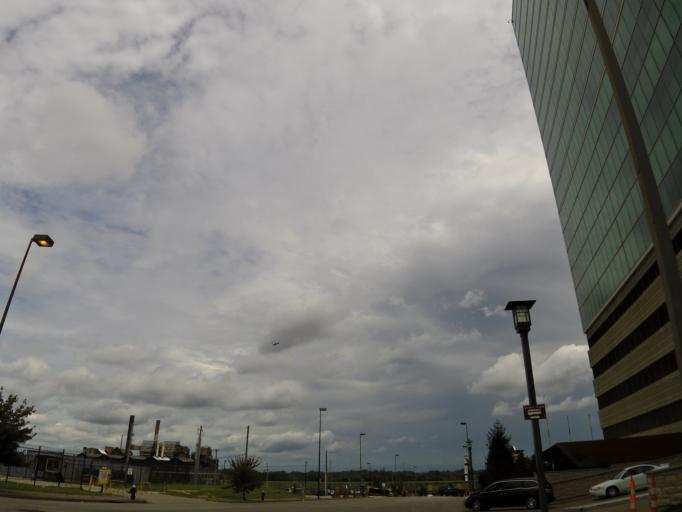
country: US
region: Missouri
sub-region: City of Saint Louis
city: St. Louis
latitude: 38.6341
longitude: -90.1852
